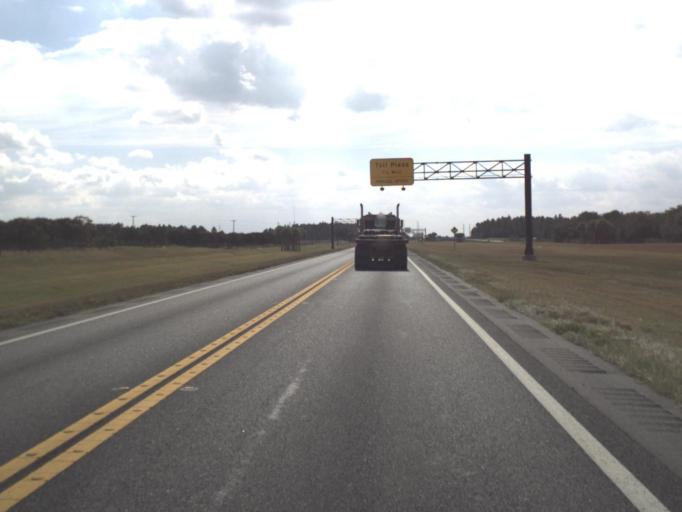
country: US
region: Florida
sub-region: Polk County
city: Polk City
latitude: 28.1185
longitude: -81.8346
